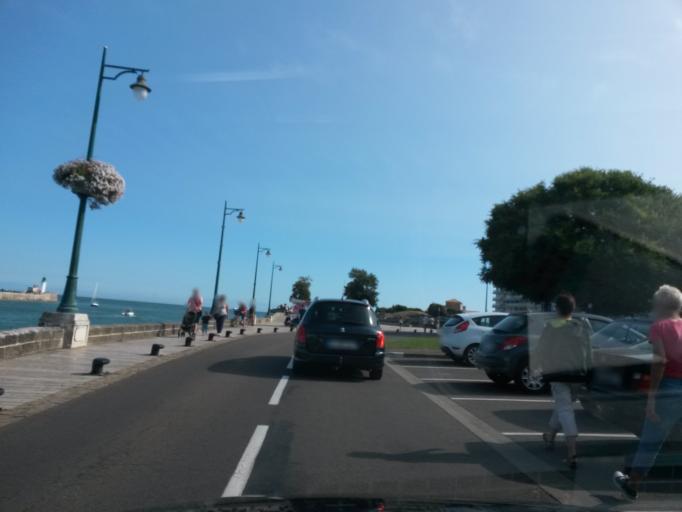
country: FR
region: Pays de la Loire
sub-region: Departement de la Vendee
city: Les Sables-d'Olonne
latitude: 46.4929
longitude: -1.7951
